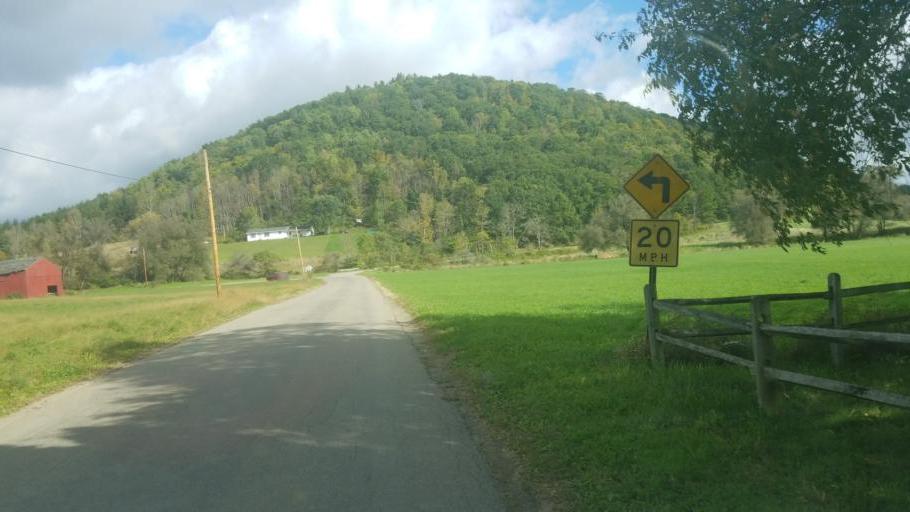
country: US
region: New York
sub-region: Cattaraugus County
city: Weston Mills
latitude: 42.1351
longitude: -78.3442
